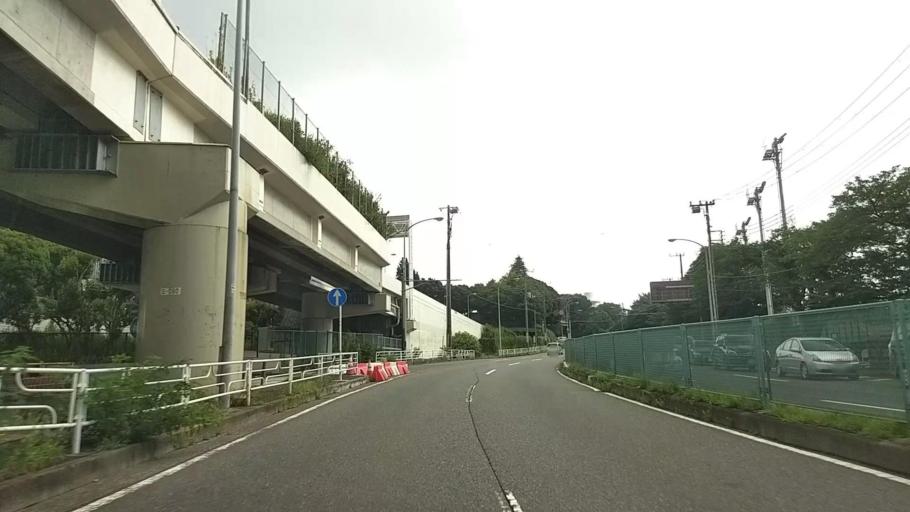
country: JP
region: Kanagawa
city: Yokohama
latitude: 35.4721
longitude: 139.6039
